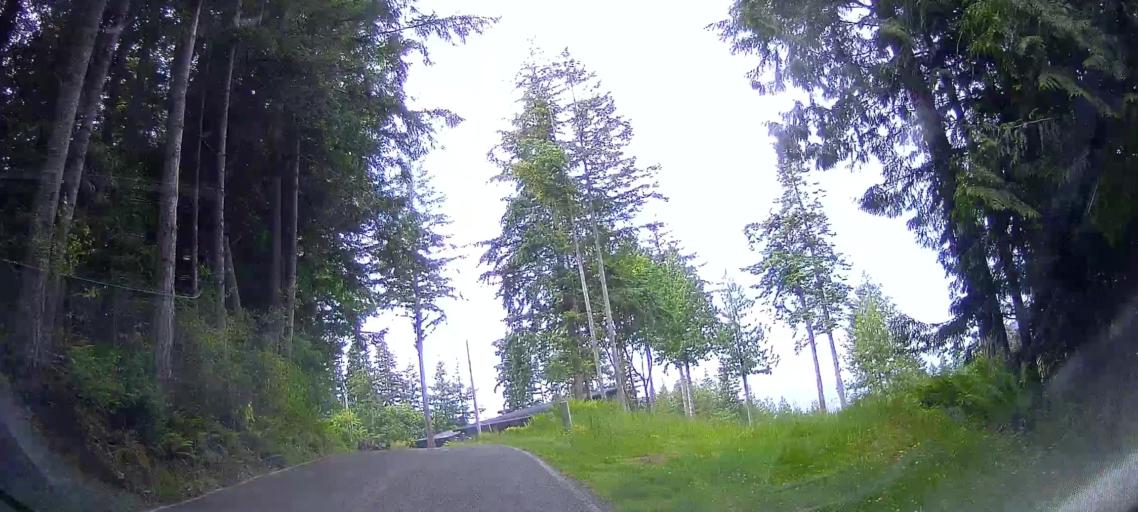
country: US
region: Washington
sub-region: Whatcom County
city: Bellingham
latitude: 48.6623
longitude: -122.4950
